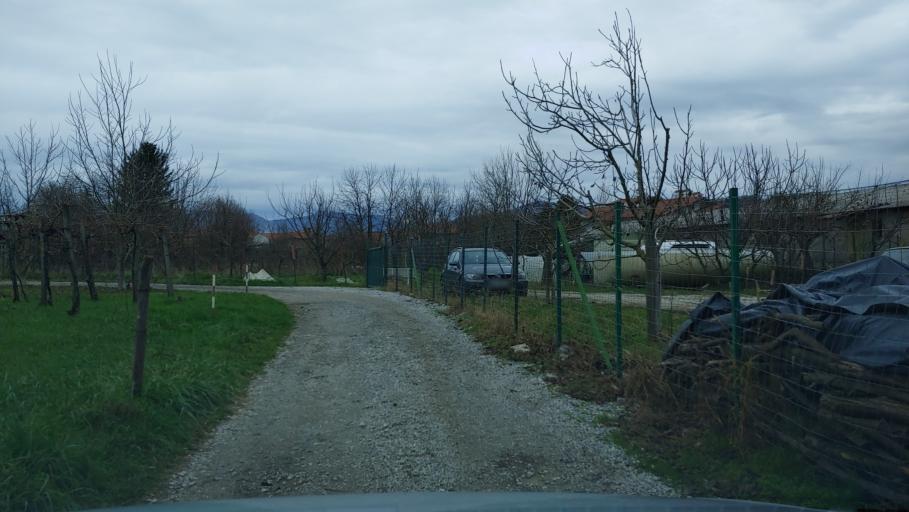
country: SI
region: Sempeter-Vrtojba
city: Vrtojba
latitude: 45.9116
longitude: 13.6394
